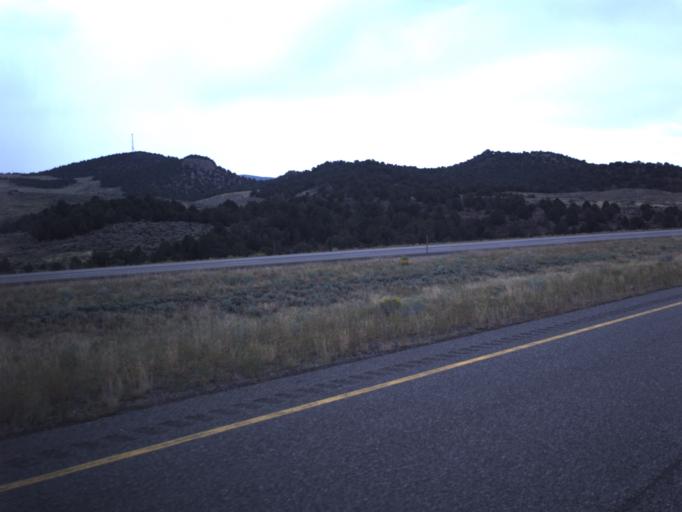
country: US
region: Utah
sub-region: Sevier County
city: Monroe
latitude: 38.5511
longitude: -112.3947
